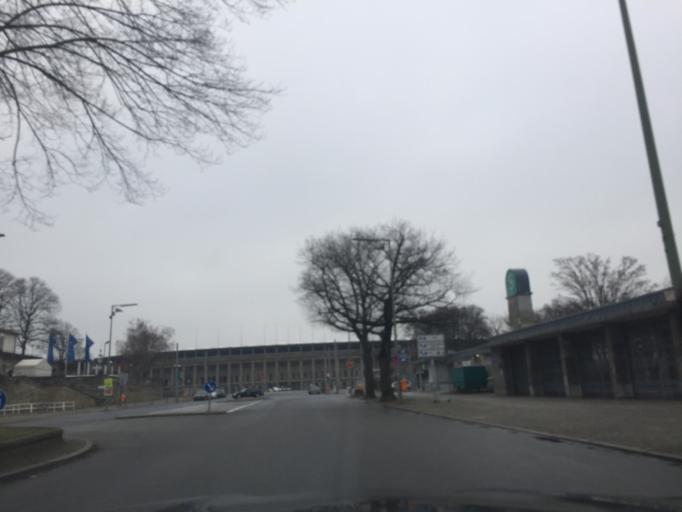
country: DE
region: Berlin
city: Haselhorst
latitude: 52.5112
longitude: 13.2408
